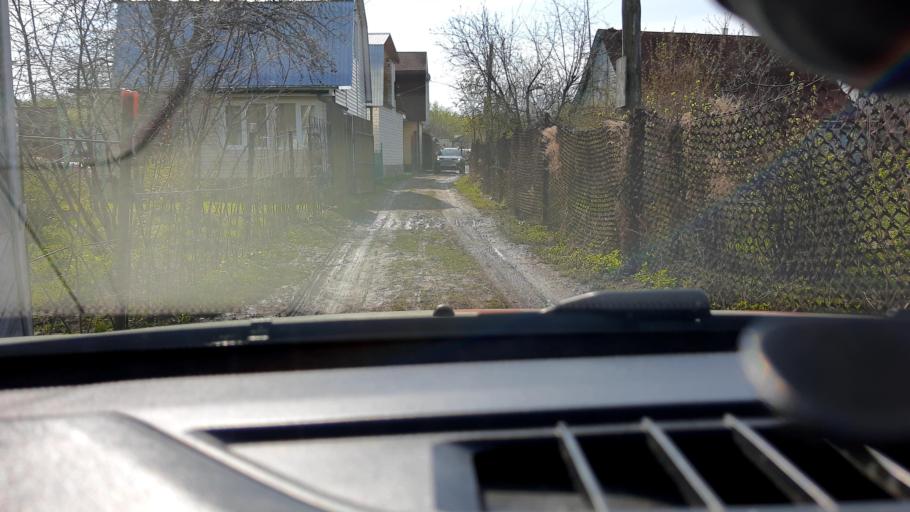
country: RU
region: Nizjnij Novgorod
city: Gorbatovka
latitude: 56.2786
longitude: 43.7865
